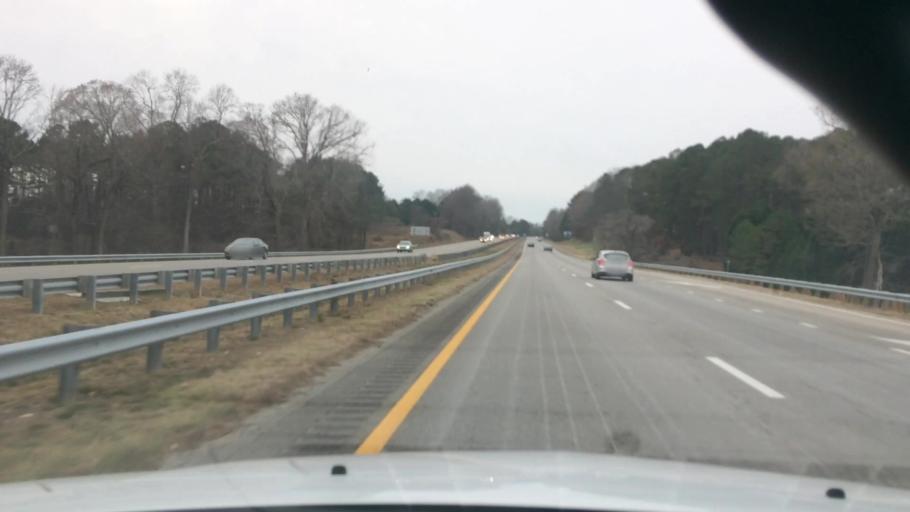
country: US
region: North Carolina
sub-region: Nash County
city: Red Oak
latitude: 35.9798
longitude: -77.9023
